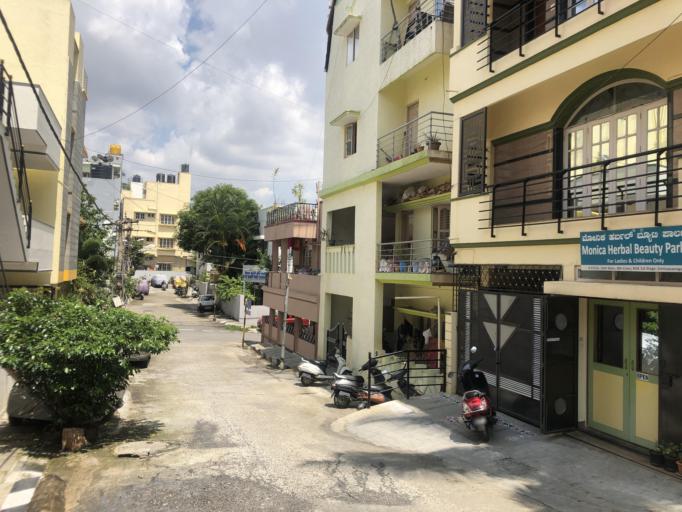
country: IN
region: Karnataka
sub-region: Bangalore Urban
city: Bangalore
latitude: 12.9358
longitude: 77.5502
